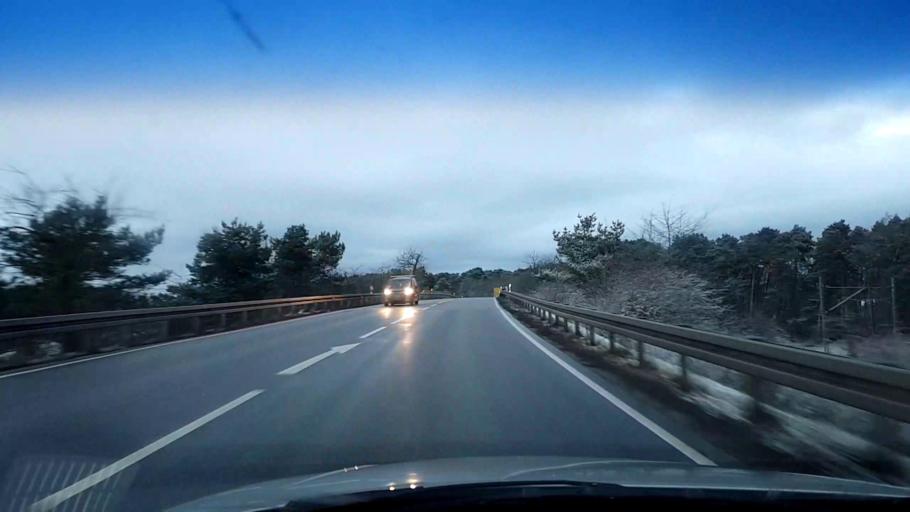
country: DE
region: Bavaria
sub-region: Upper Franconia
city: Hirschaid
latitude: 49.8258
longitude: 10.9829
